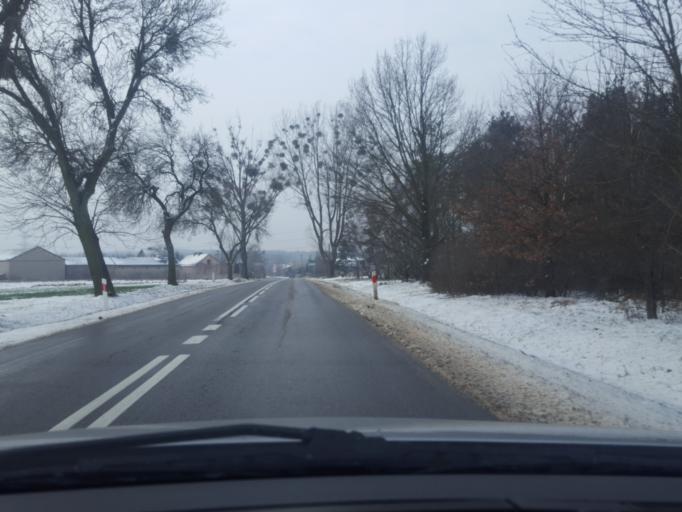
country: PL
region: Lodz Voivodeship
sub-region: Powiat brzezinski
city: Brzeziny
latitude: 51.8321
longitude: 19.7964
